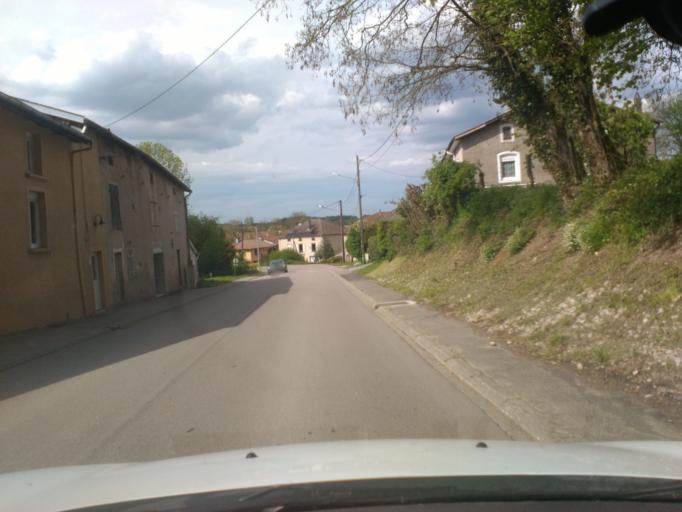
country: FR
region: Lorraine
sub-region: Departement des Vosges
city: Mirecourt
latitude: 48.2642
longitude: 6.1433
